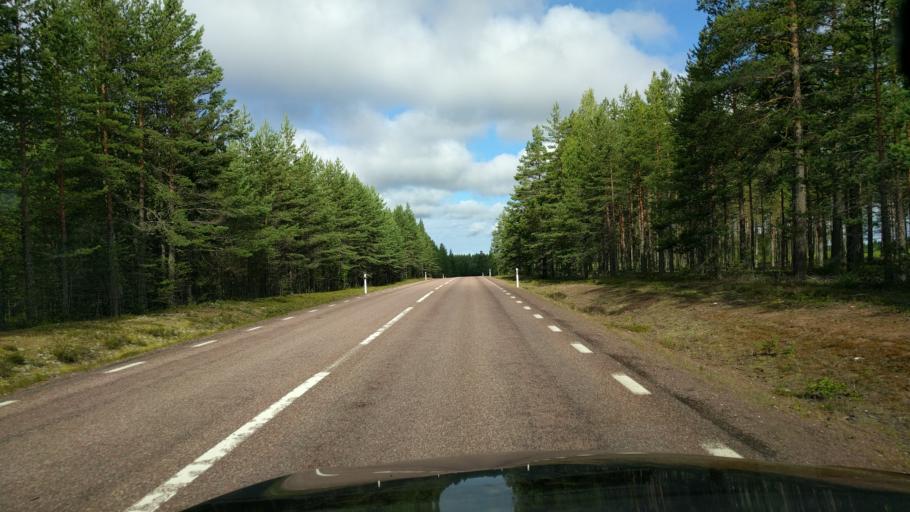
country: SE
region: Dalarna
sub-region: Mora Kommun
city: Mora
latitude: 61.0570
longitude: 14.4177
